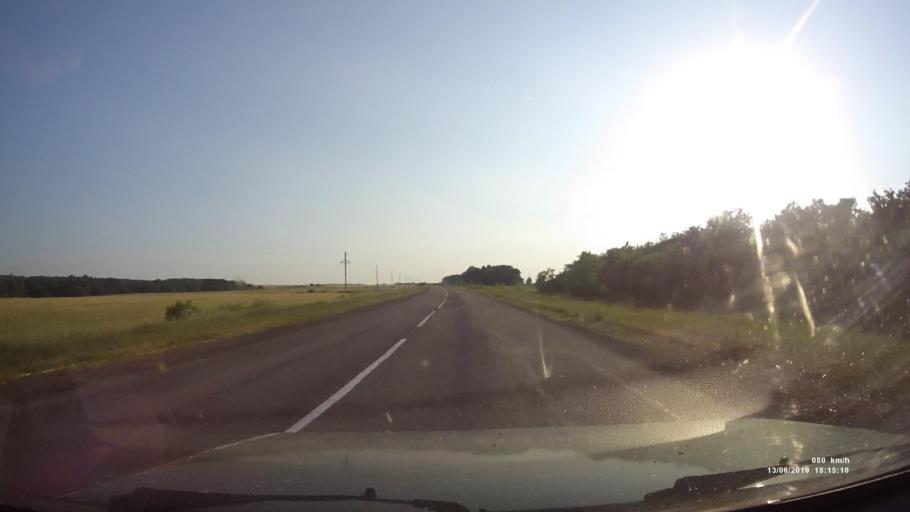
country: RU
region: Rostov
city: Kazanskaya
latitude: 49.9325
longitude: 41.3621
